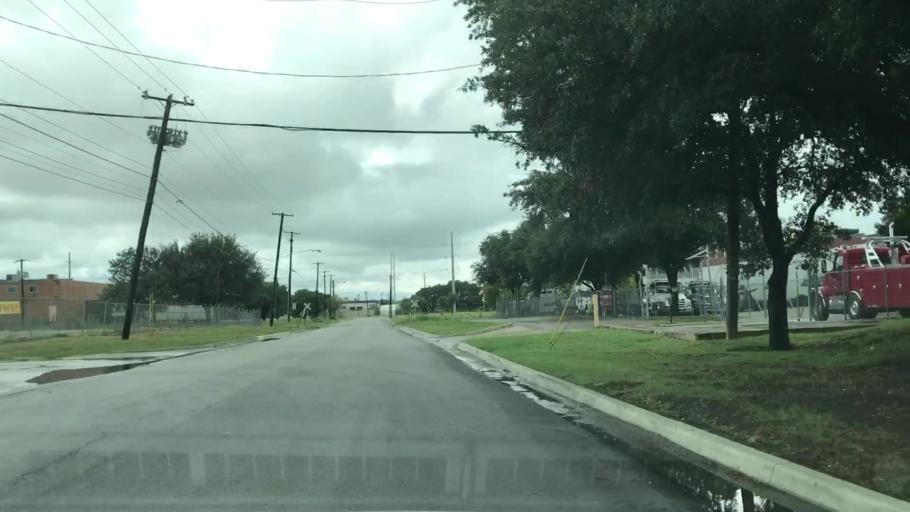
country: US
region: Texas
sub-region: Dallas County
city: Irving
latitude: 32.8239
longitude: -96.8857
